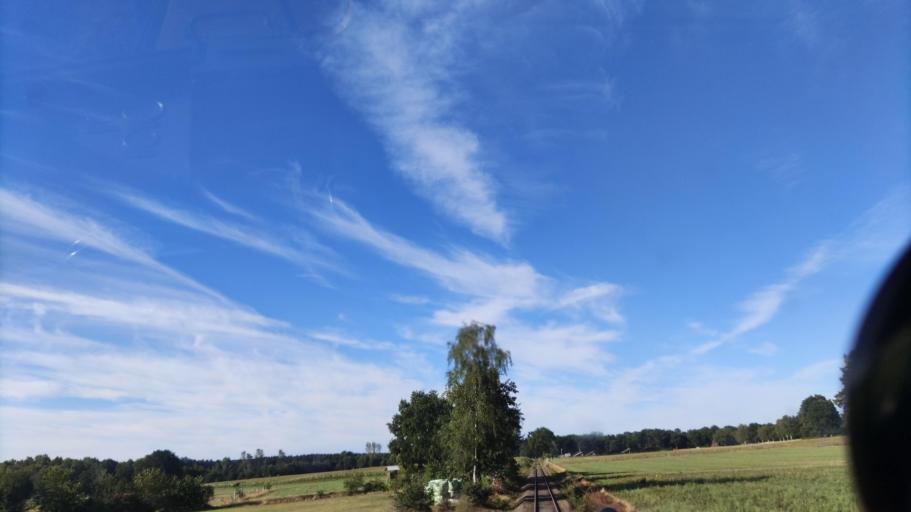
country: DE
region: Lower Saxony
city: Soderstorf
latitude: 53.1293
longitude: 10.1315
